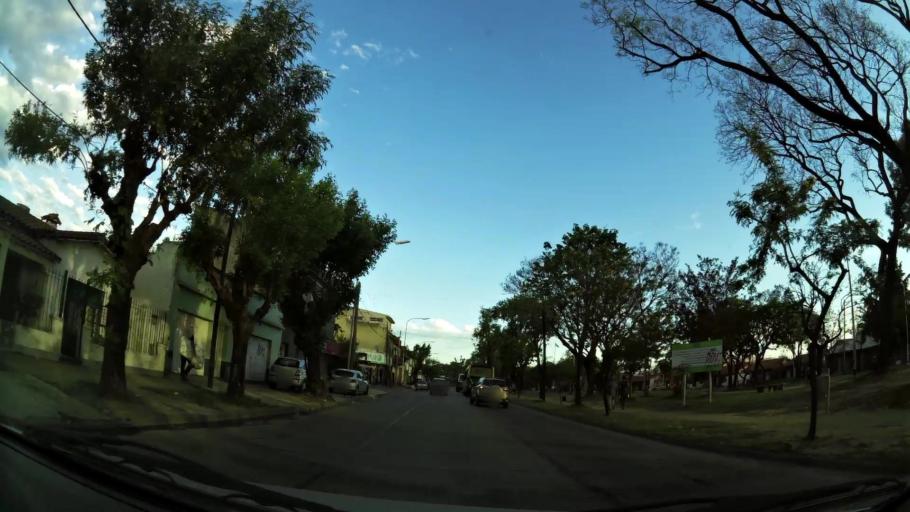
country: AR
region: Buenos Aires
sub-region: Partido de Avellaneda
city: Avellaneda
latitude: -34.7002
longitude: -58.3424
